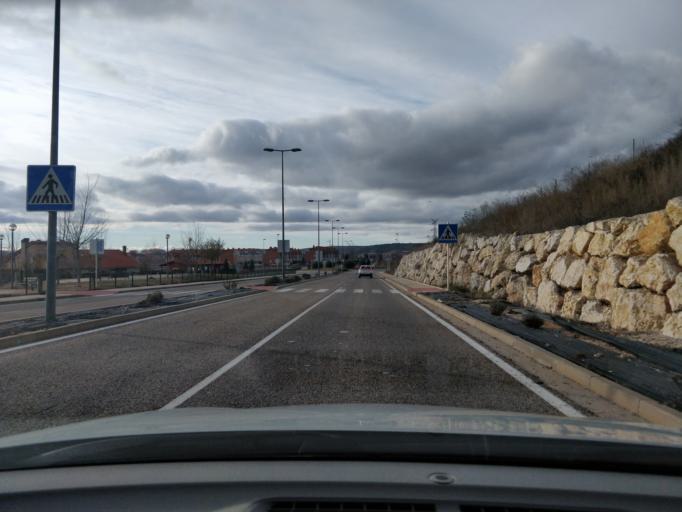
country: ES
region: Castille and Leon
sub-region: Provincia de Burgos
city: Villalbilla de Burgos
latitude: 42.3514
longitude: -3.7384
